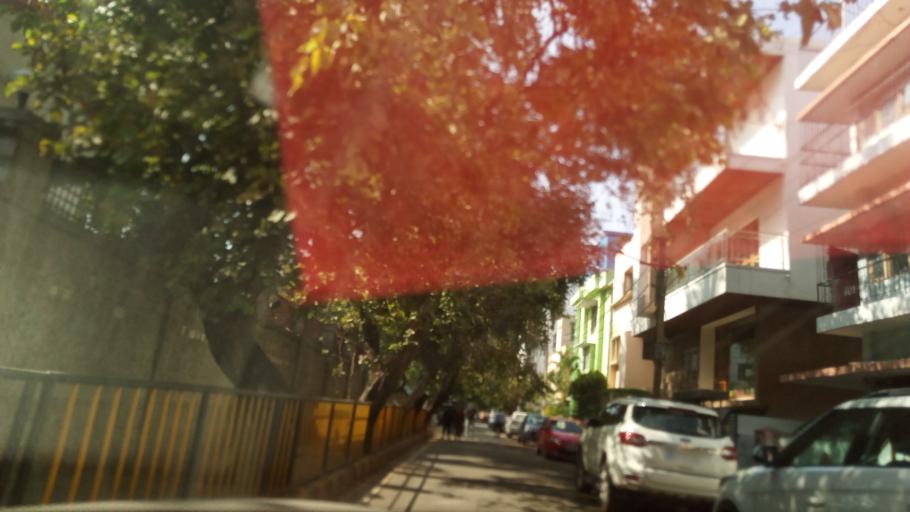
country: IN
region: Karnataka
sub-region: Bangalore Urban
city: Bangalore
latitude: 13.0031
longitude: 77.5832
